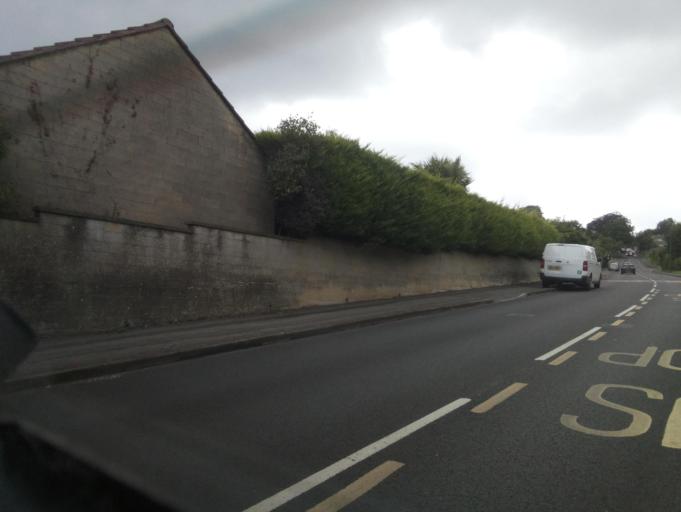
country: GB
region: England
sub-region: Bath and North East Somerset
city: Bath
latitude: 51.4019
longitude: -2.3958
